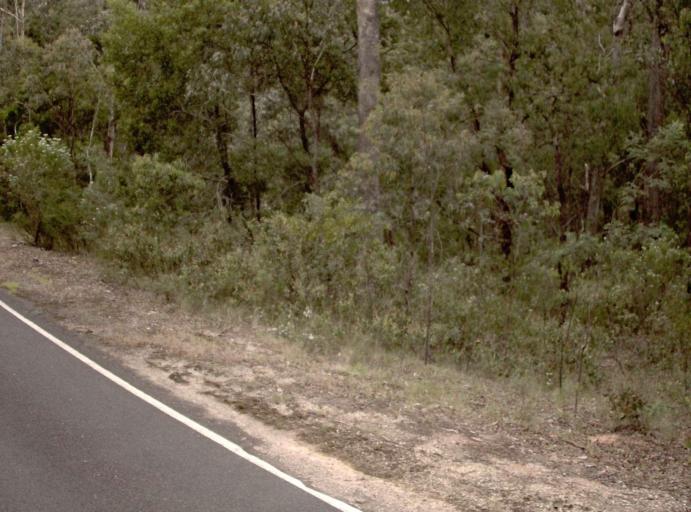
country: AU
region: Victoria
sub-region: East Gippsland
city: Bairnsdale
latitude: -37.6351
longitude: 147.2267
